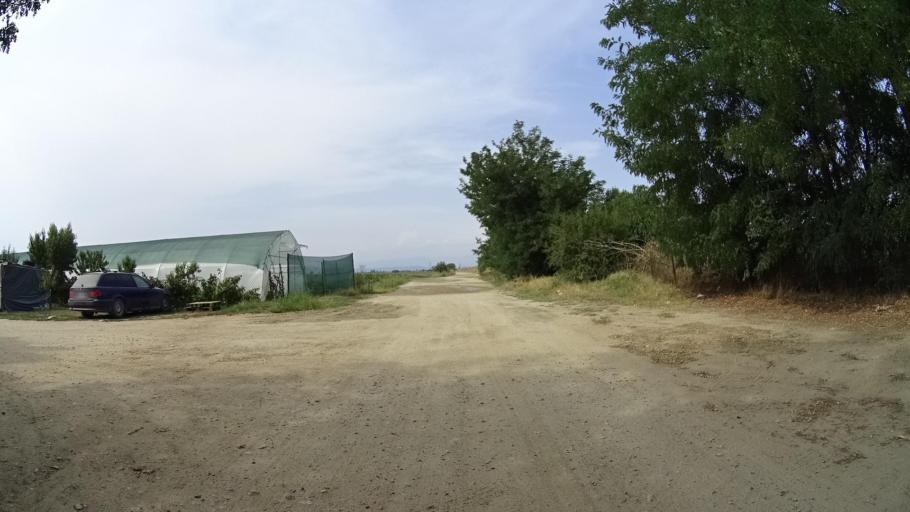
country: BG
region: Plovdiv
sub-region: Obshtina Kaloyanovo
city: Kaloyanovo
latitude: 42.3055
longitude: 24.7993
